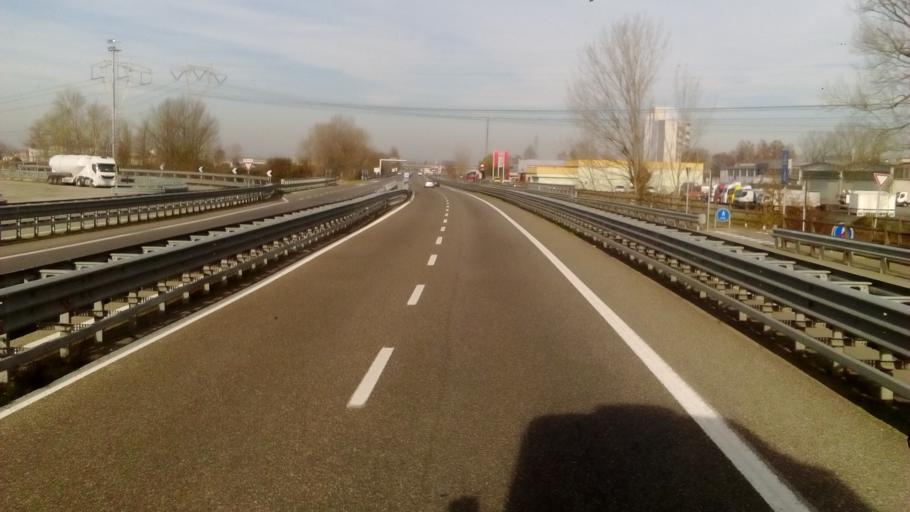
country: IT
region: Lombardy
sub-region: Provincia di Lodi
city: Guardamiglio
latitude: 45.1153
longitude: 9.6877
